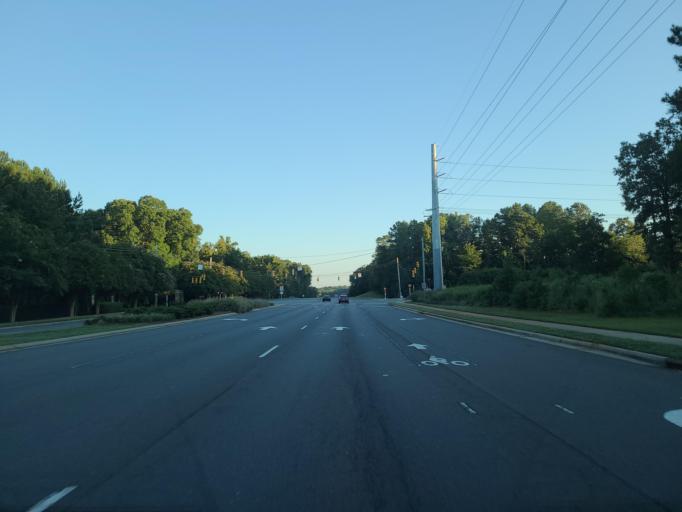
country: US
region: North Carolina
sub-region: Union County
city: Weddington
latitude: 35.0301
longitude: -80.7647
